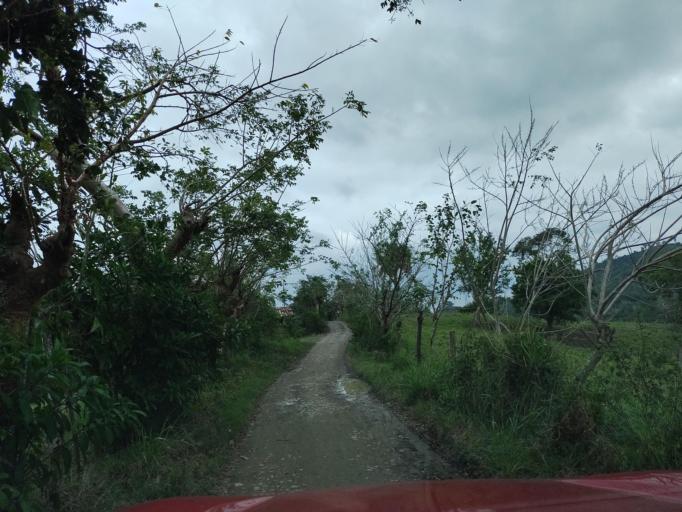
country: MX
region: Veracruz
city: Coatzintla
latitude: 20.4585
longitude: -97.4159
